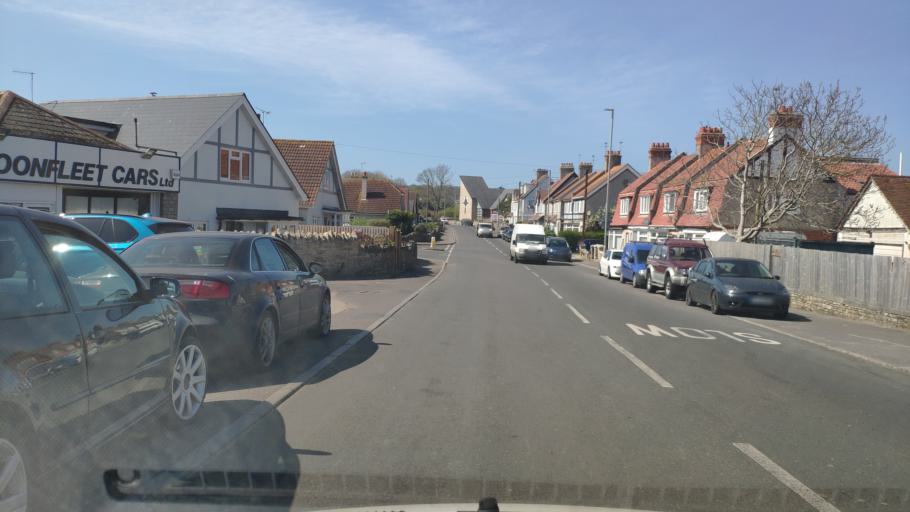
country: GB
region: England
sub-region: Dorset
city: Swanage
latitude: 50.6118
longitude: -1.9741
